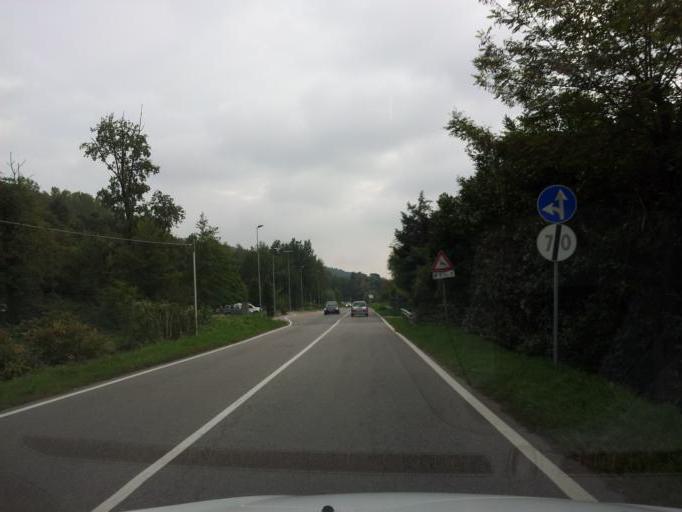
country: IT
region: Lombardy
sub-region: Provincia di Varese
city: Varano Borghi
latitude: 45.7631
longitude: 8.7018
